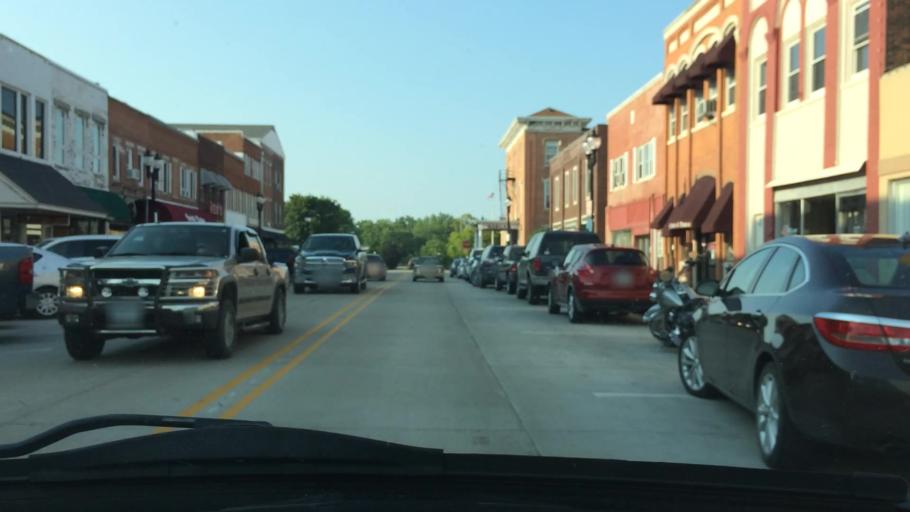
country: US
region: Iowa
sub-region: Henry County
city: Mount Pleasant
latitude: 40.9668
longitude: -91.5546
